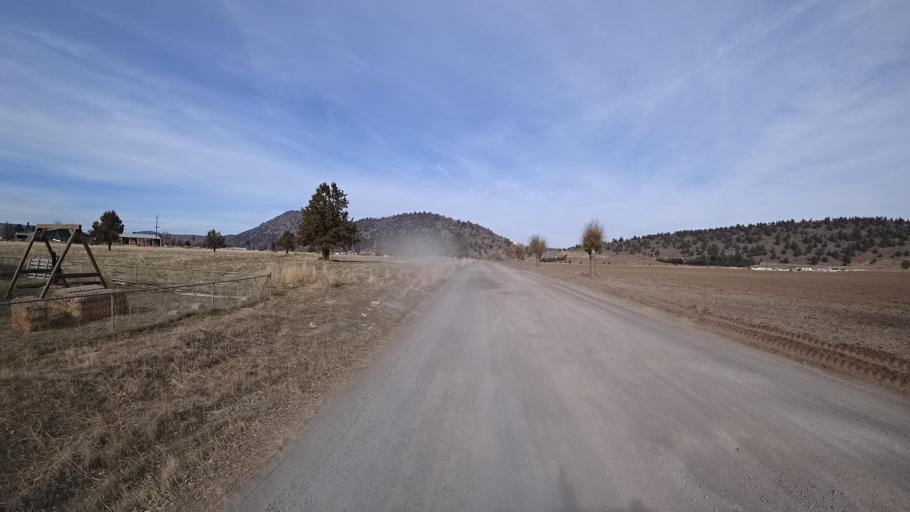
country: US
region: Oregon
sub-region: Klamath County
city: Klamath Falls
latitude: 41.9631
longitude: -121.9115
